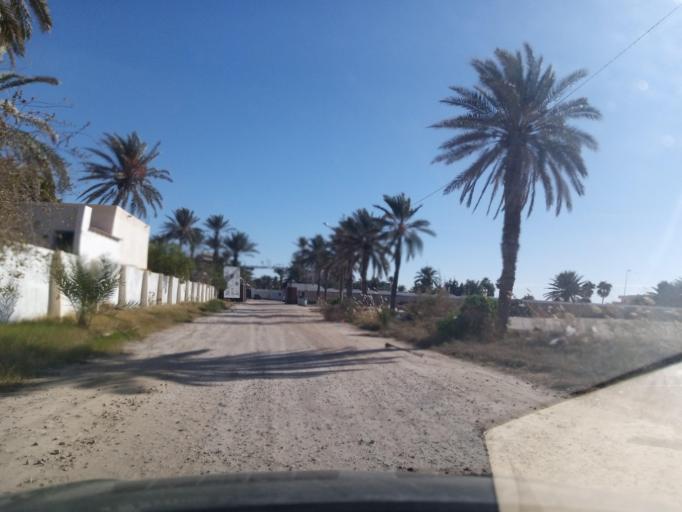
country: TN
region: Qabis
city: Gabes
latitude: 33.8906
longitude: 10.1148
